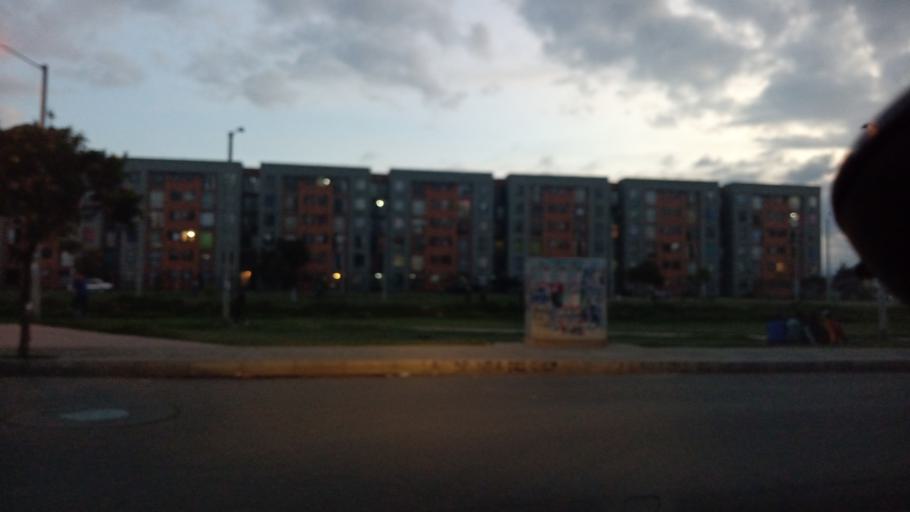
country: CO
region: Cundinamarca
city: Soacha
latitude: 4.5795
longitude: -74.2333
